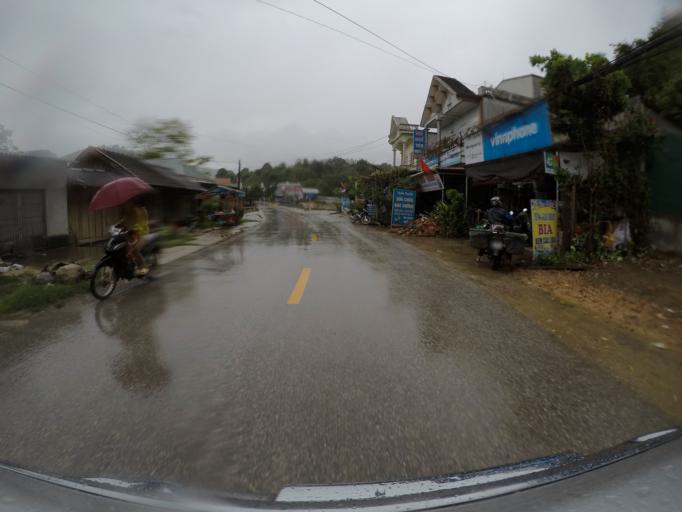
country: VN
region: Lai Chau
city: Than Uyen
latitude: 22.0725
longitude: 103.8526
